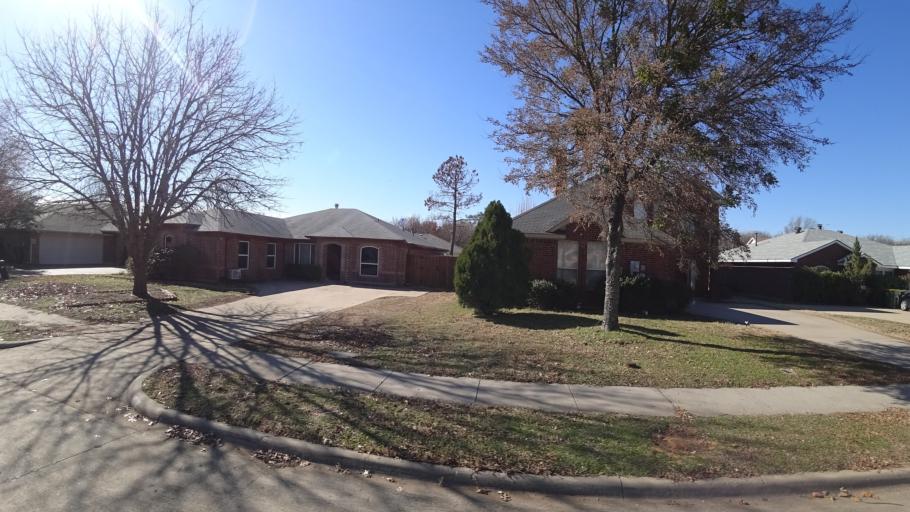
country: US
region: Texas
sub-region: Denton County
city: Lewisville
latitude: 33.0173
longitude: -97.0069
